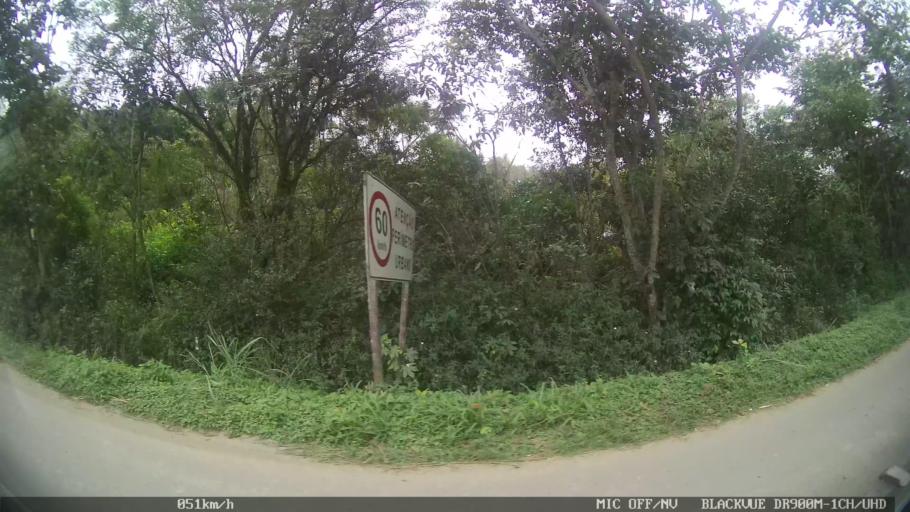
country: BR
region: Santa Catarina
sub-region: Joinville
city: Joinville
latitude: -26.2016
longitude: -48.9159
